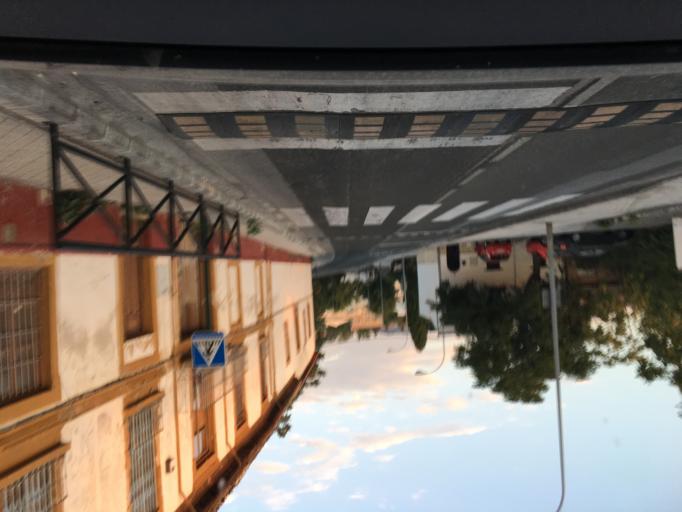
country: ES
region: Andalusia
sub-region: Provincia de Granada
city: Viznar
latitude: 37.2022
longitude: -3.5649
